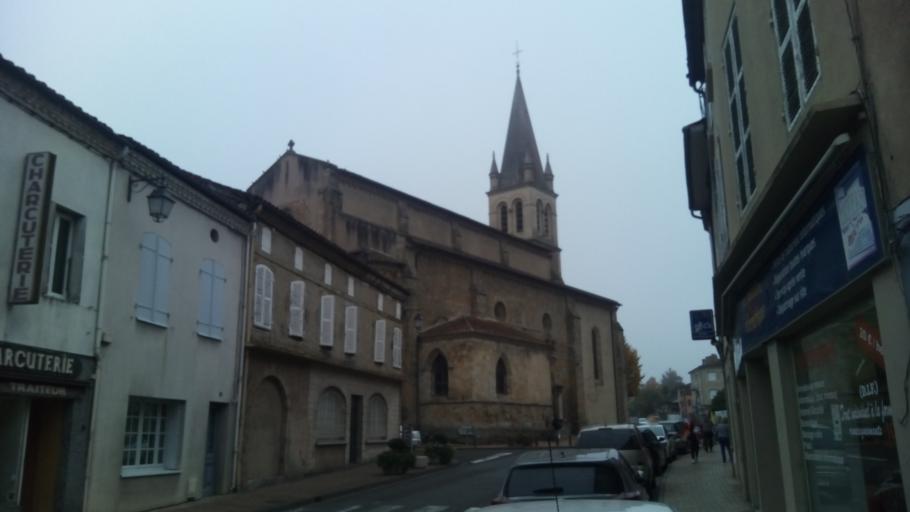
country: FR
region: Midi-Pyrenees
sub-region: Departement du Gers
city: Nogaro
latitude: 43.7577
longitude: -0.0347
